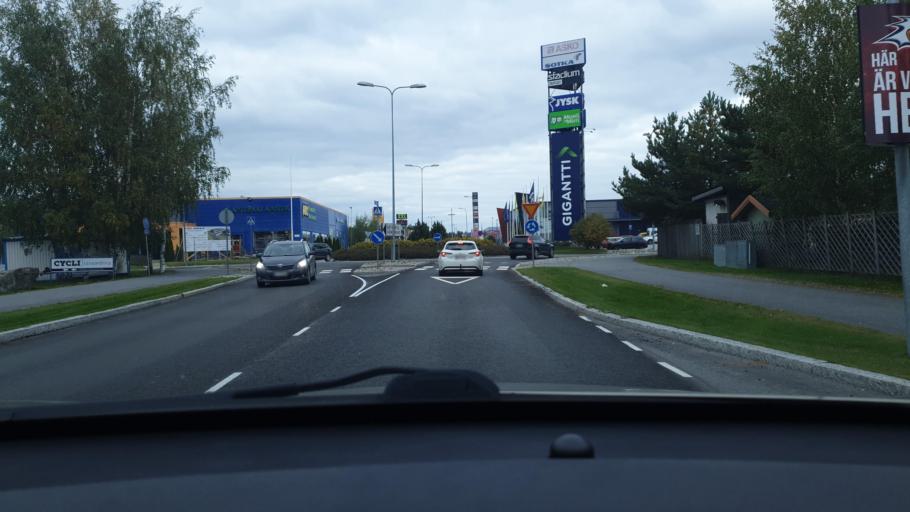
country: FI
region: Ostrobothnia
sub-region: Vaasa
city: Korsholm
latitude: 63.1100
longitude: 21.6510
